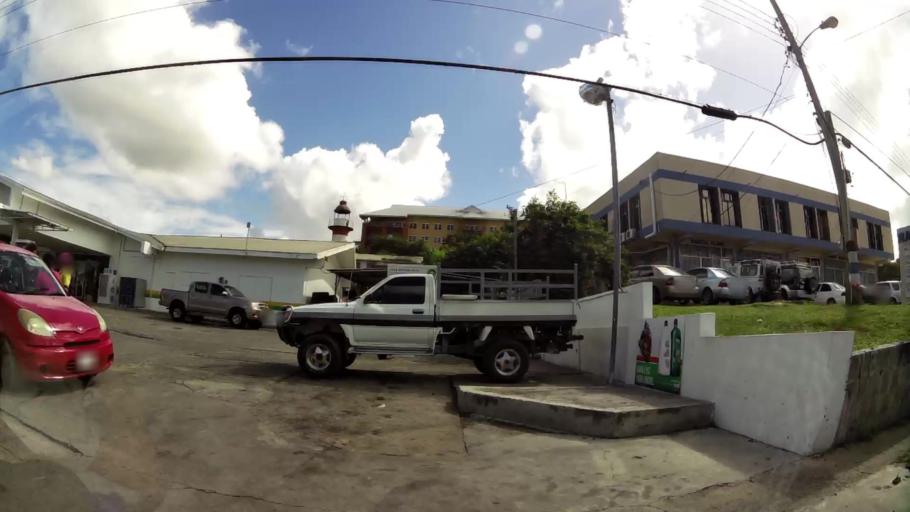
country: AG
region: Saint John
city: Saint John's
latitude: 17.1179
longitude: -61.8403
